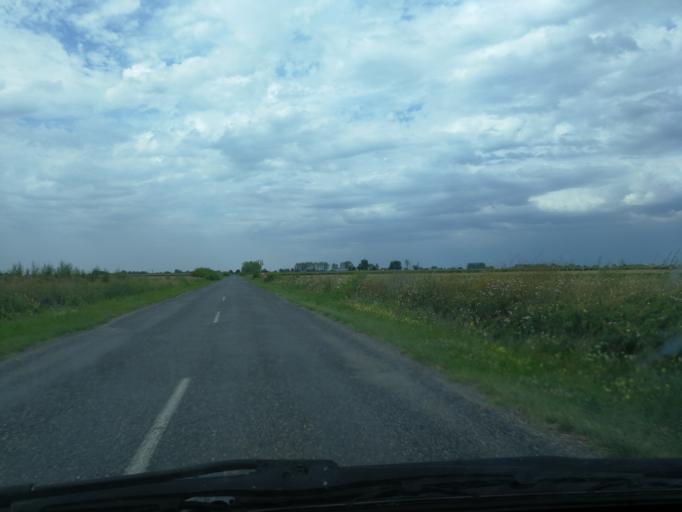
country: HU
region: Bacs-Kiskun
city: Kalocsa
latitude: 46.4837
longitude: 19.0509
